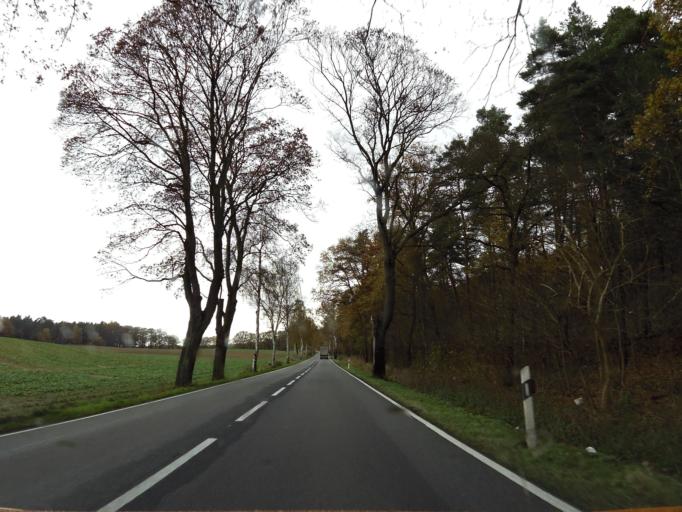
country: DE
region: Saxony-Anhalt
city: Kalbe
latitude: 52.6225
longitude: 11.3164
